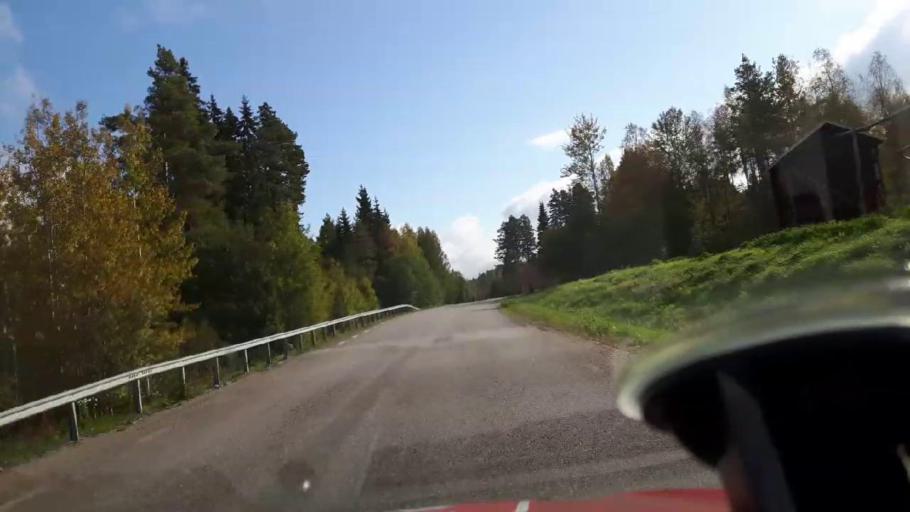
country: SE
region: Gaevleborg
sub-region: Ljusdals Kommun
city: Ljusdal
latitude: 61.7684
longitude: 16.0224
